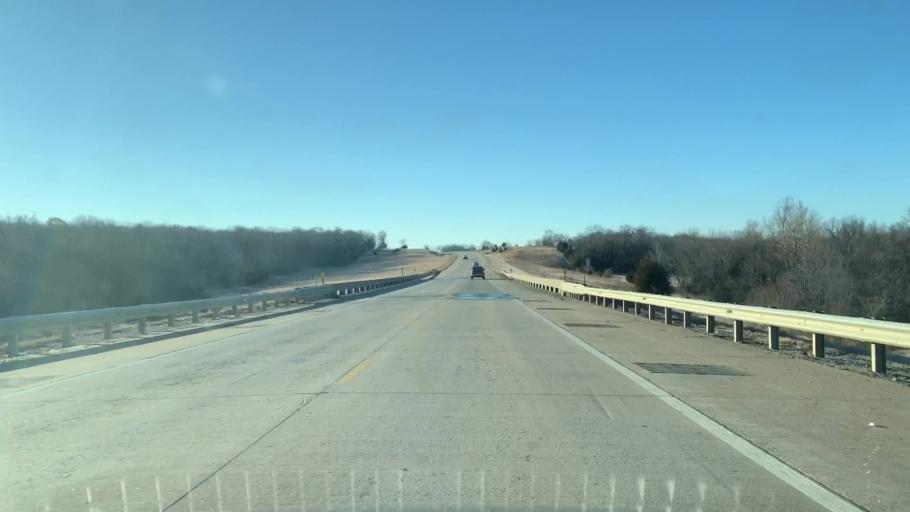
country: US
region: Kansas
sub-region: Crawford County
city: Arma
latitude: 37.5848
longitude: -94.7055
